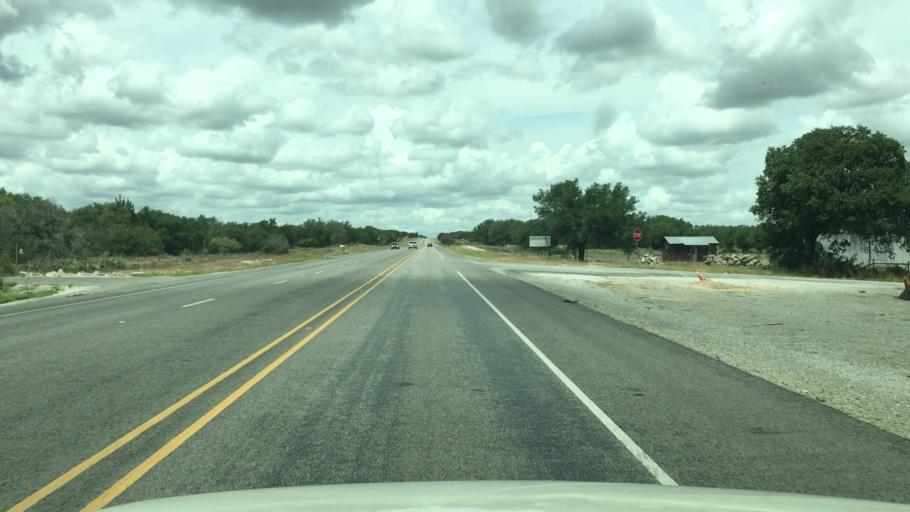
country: US
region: Texas
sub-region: McCulloch County
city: Brady
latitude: 31.0275
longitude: -99.2251
